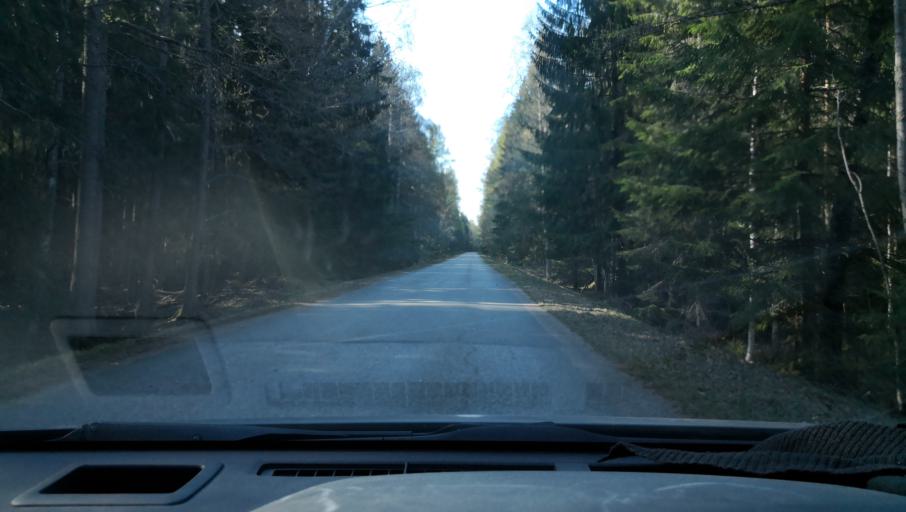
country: SE
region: Uppsala
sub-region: Heby Kommun
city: Tarnsjo
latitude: 60.2750
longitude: 16.8984
